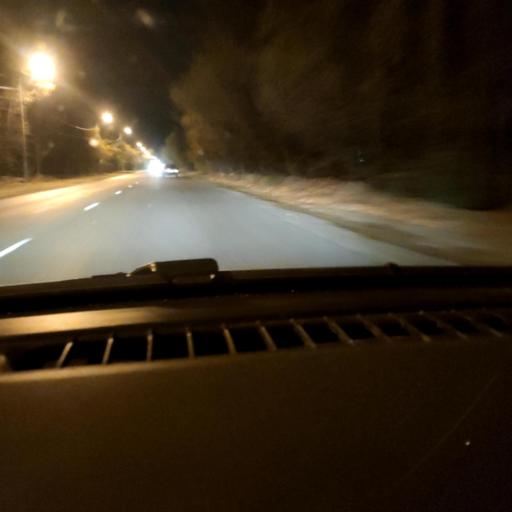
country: RU
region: Voronezj
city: Pridonskoy
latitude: 51.6871
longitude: 39.1009
